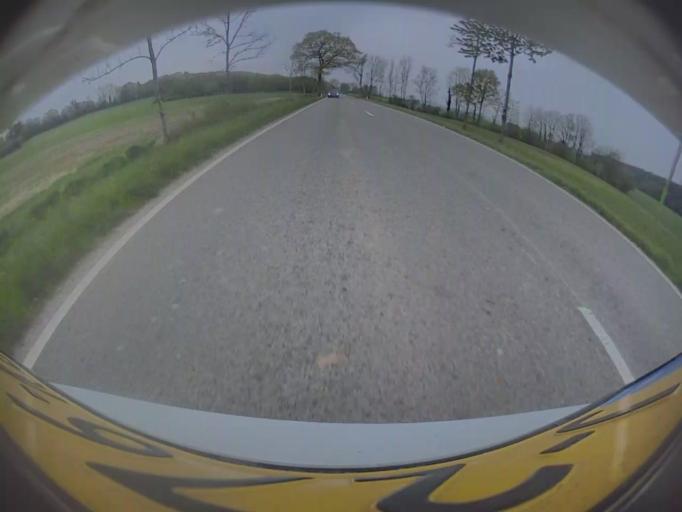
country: BE
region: Wallonia
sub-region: Province de Liege
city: Ferrieres
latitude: 50.4197
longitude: 5.5799
